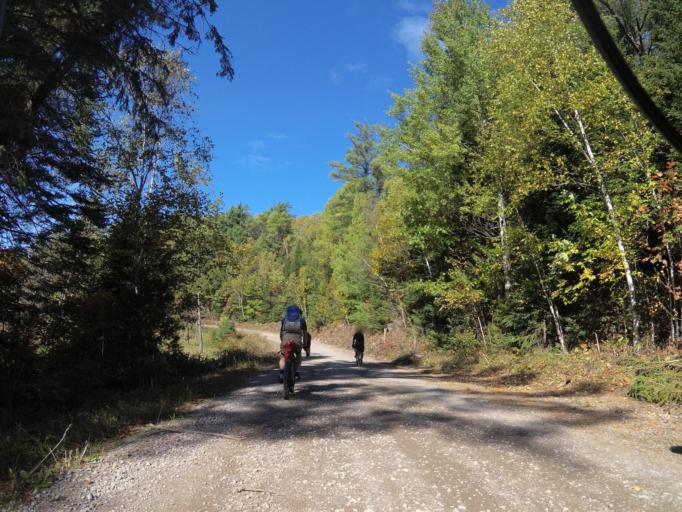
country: CA
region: Ontario
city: Renfrew
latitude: 45.3241
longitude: -77.0407
